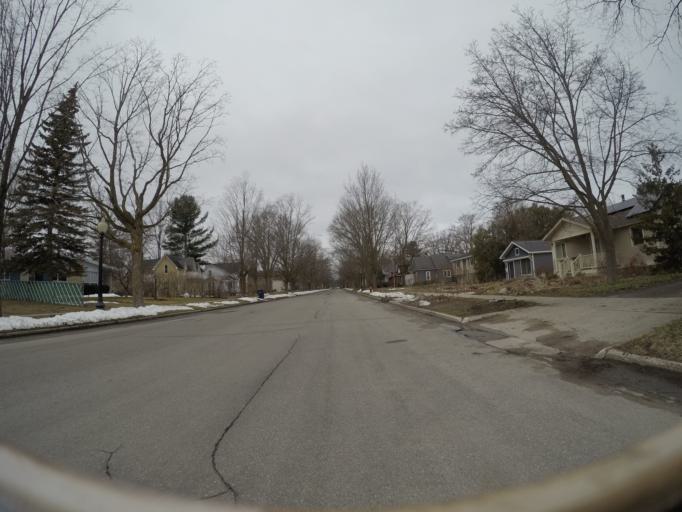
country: US
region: Michigan
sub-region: Grand Traverse County
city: Traverse City
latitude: 44.7606
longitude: -85.6009
